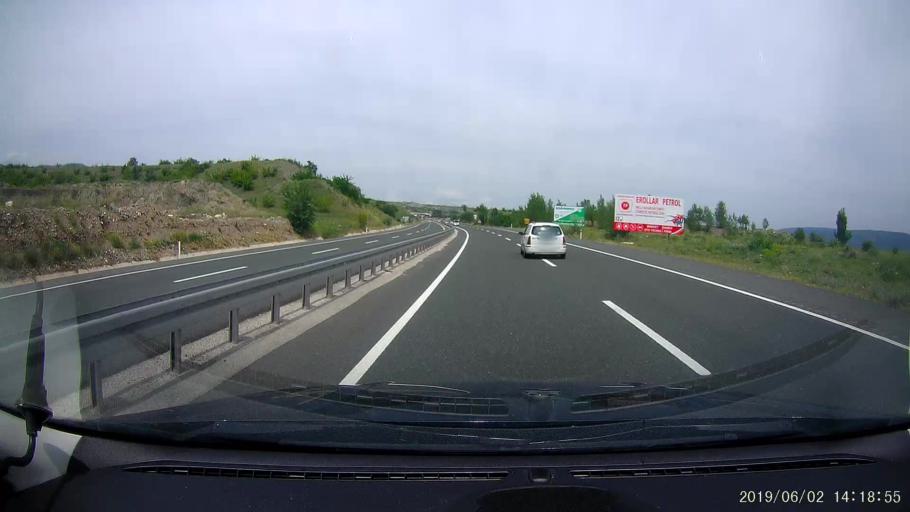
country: TR
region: Kastamonu
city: Tosya
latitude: 40.9583
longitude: 33.9669
